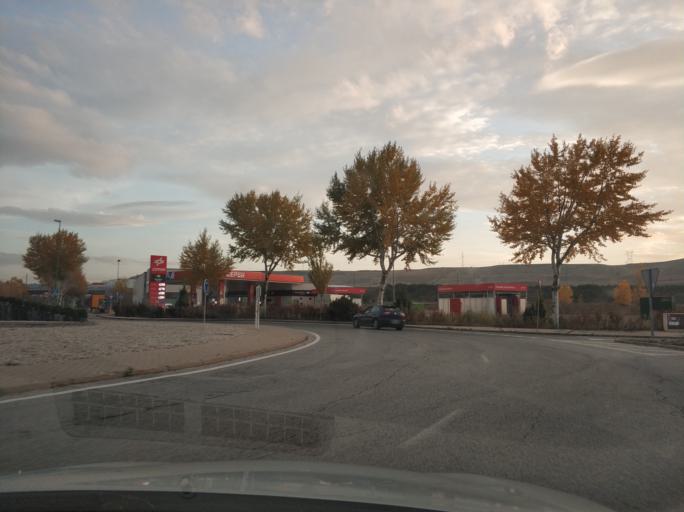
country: ES
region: Castille and Leon
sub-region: Provincia de Burgos
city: Sotragero
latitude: 42.3710
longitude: -3.7184
